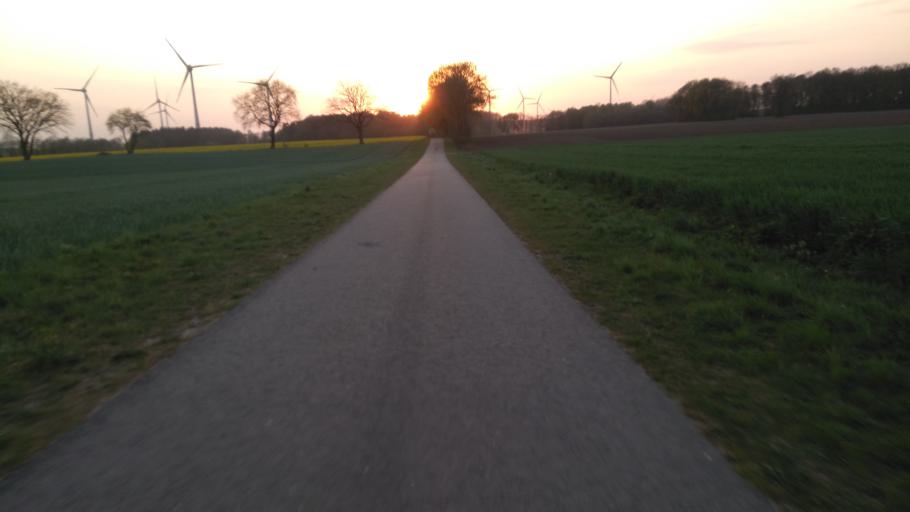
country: DE
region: Lower Saxony
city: Harsefeld
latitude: 53.4931
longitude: 9.5089
